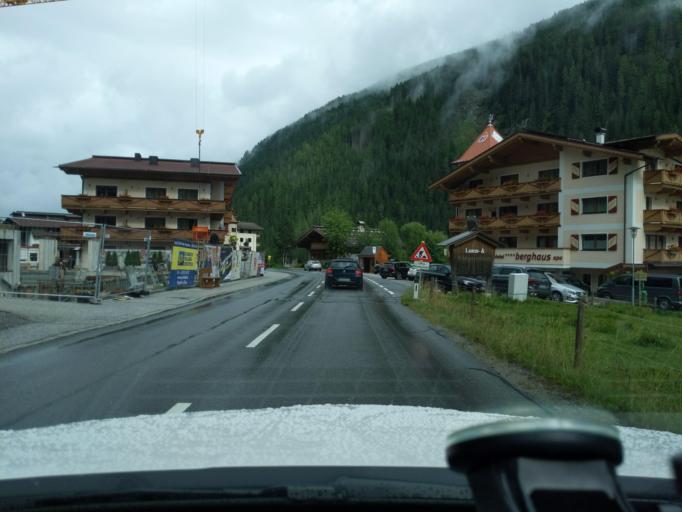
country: AT
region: Tyrol
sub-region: Politischer Bezirk Innsbruck Land
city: Schmirn
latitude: 47.1265
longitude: 11.6956
